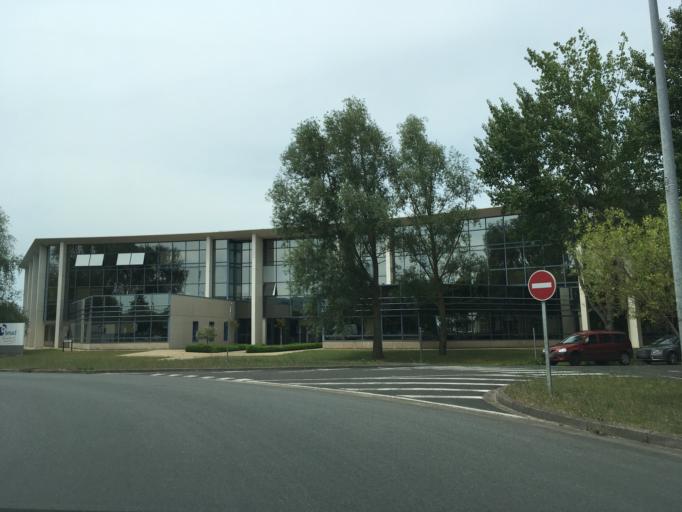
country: FR
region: Poitou-Charentes
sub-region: Departement des Deux-Sevres
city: Niort
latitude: 46.3327
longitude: -0.4859
